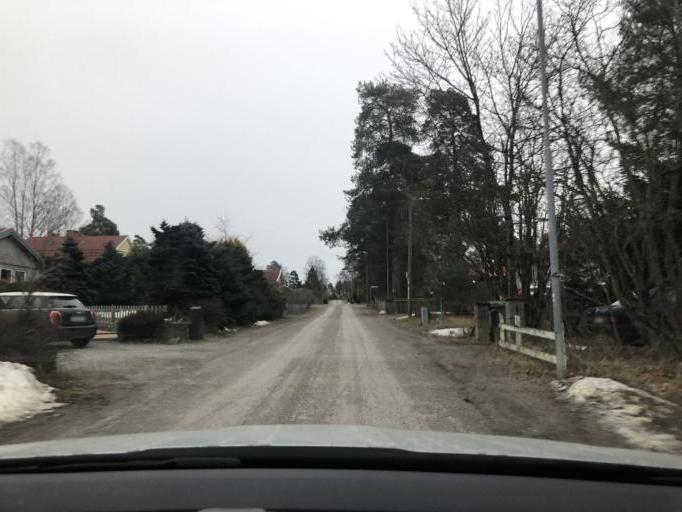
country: SE
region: Stockholm
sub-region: Botkyrka Kommun
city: Tullinge
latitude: 59.1960
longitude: 17.8930
